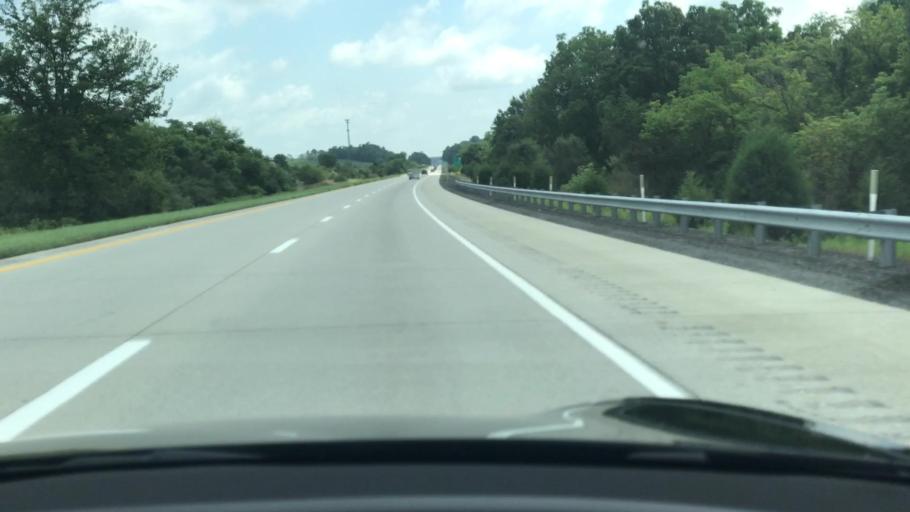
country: US
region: Pennsylvania
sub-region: Lancaster County
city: Elizabethtown
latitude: 40.1940
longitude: -76.6395
